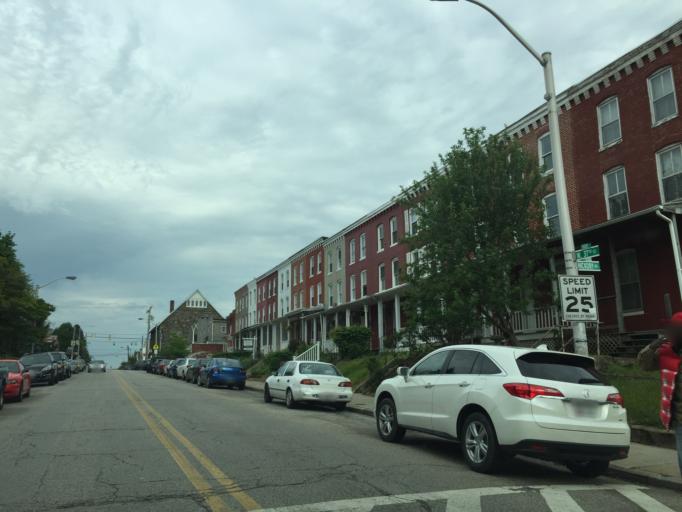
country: US
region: Maryland
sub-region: City of Baltimore
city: Baltimore
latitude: 39.3327
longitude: -76.6343
